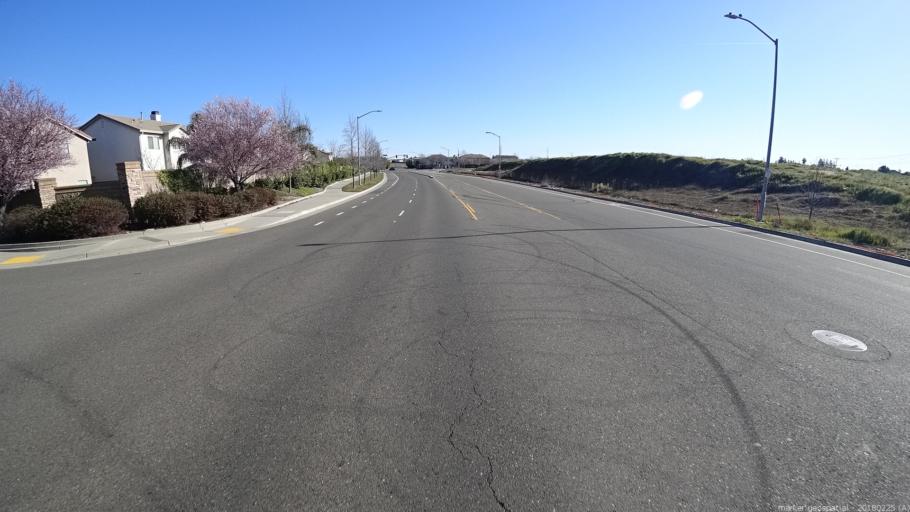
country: US
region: California
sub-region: Sacramento County
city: Antelope
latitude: 38.7045
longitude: -121.3532
